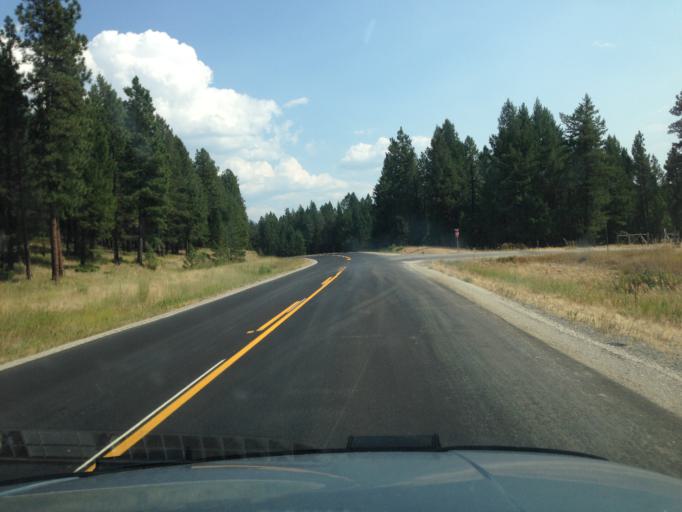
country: CA
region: British Columbia
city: Cranbrook
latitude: 49.5737
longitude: -115.5606
